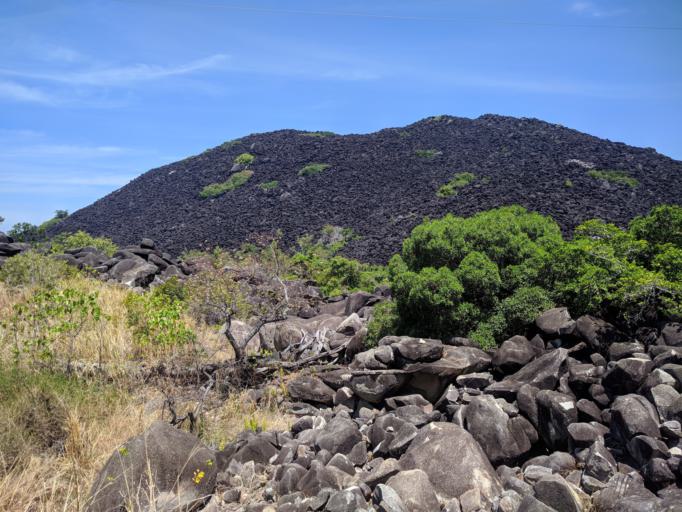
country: AU
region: Queensland
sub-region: Cook
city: Cooktown
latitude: -15.7439
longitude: 145.2491
